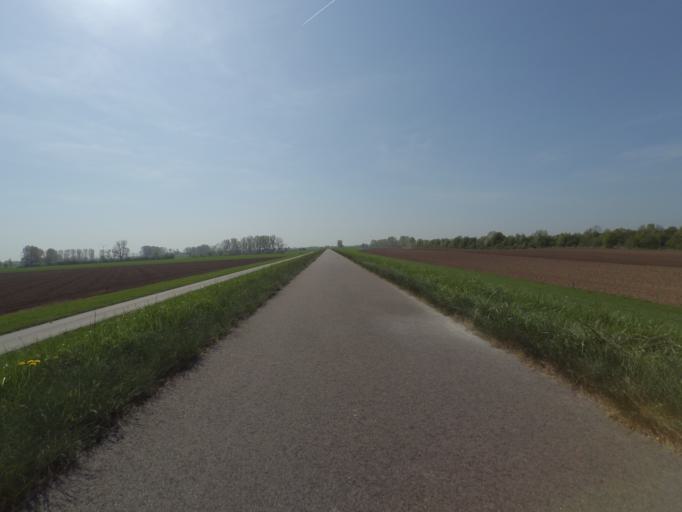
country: DE
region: North Rhine-Westphalia
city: Rees
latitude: 51.7337
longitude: 6.4374
